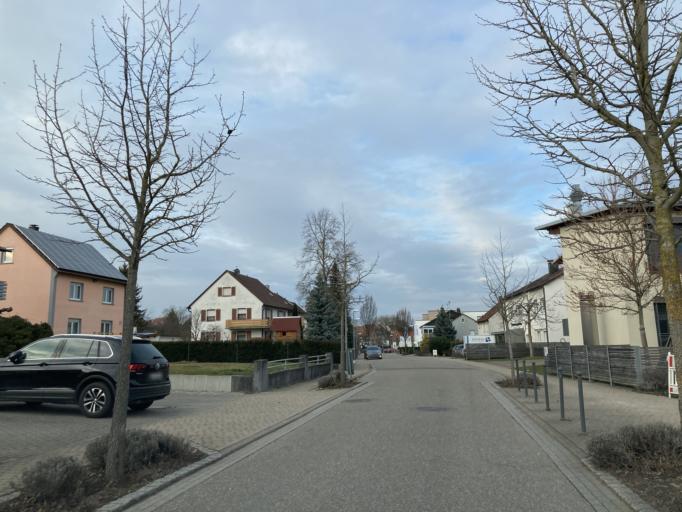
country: DE
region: Baden-Wuerttemberg
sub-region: Karlsruhe Region
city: Oberderdingen
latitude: 49.0621
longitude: 8.7963
